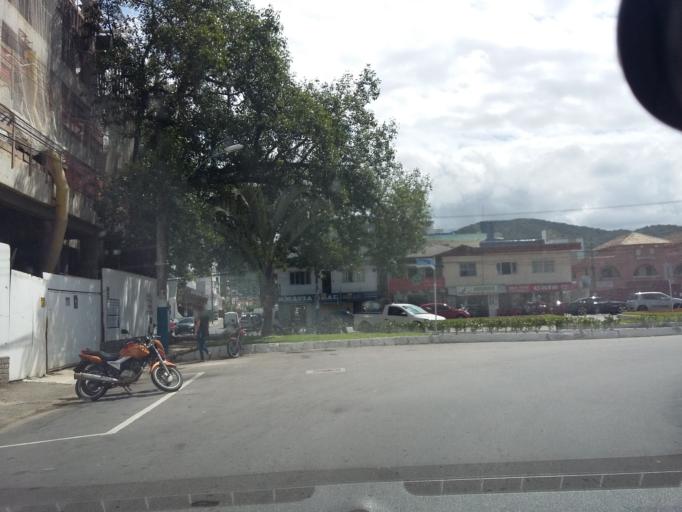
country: BR
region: Santa Catarina
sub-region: Balneario Camboriu
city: Balneario Camboriu
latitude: -26.9786
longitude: -48.6394
